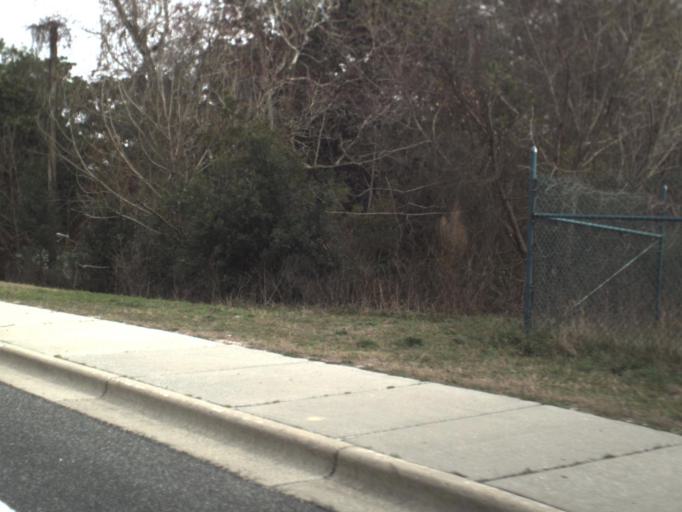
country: US
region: Florida
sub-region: Bay County
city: Laguna Beach
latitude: 30.2741
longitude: -85.9969
